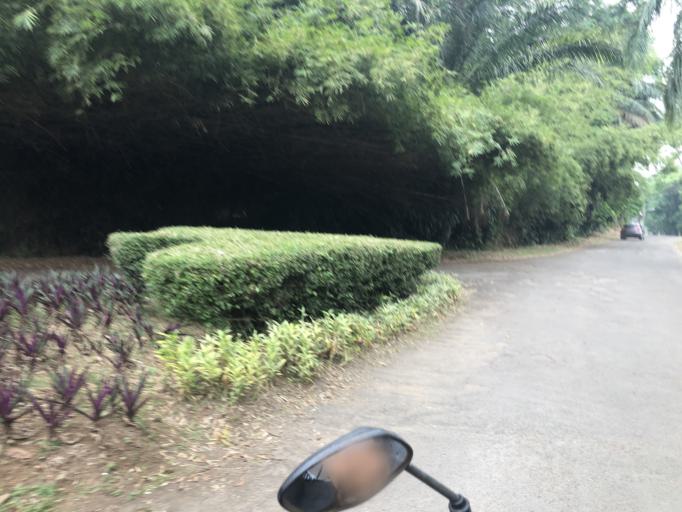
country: ID
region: West Java
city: Ciampea
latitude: -6.5539
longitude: 106.7238
